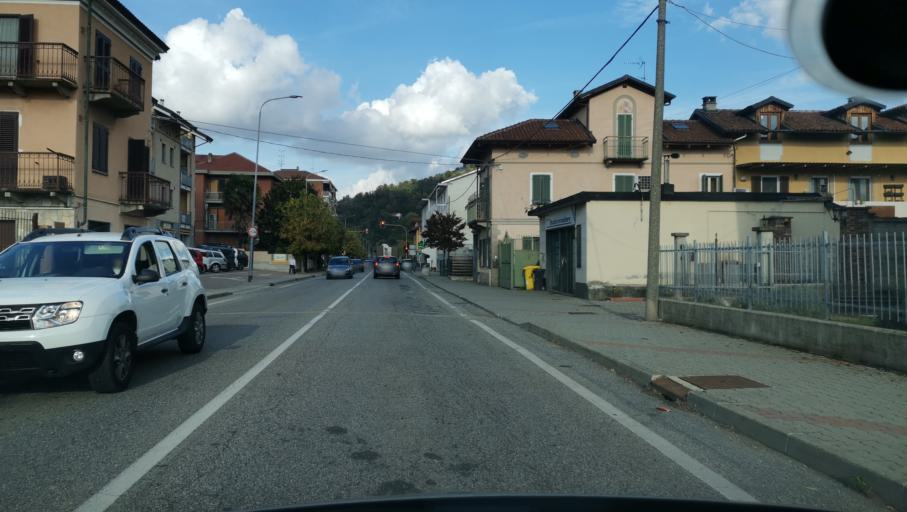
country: IT
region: Piedmont
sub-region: Provincia di Torino
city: San Raffaele Cimena
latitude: 45.1480
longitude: 7.8462
